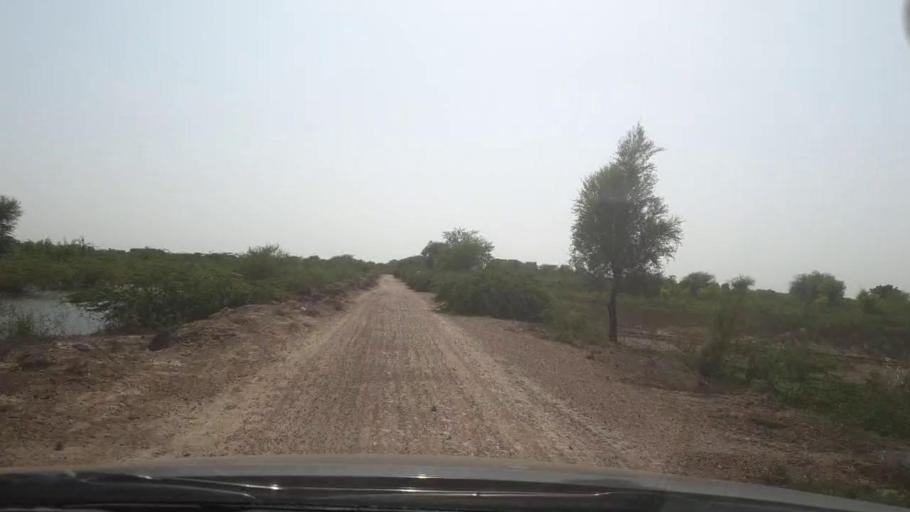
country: PK
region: Sindh
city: Naukot
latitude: 24.7858
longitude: 69.2013
